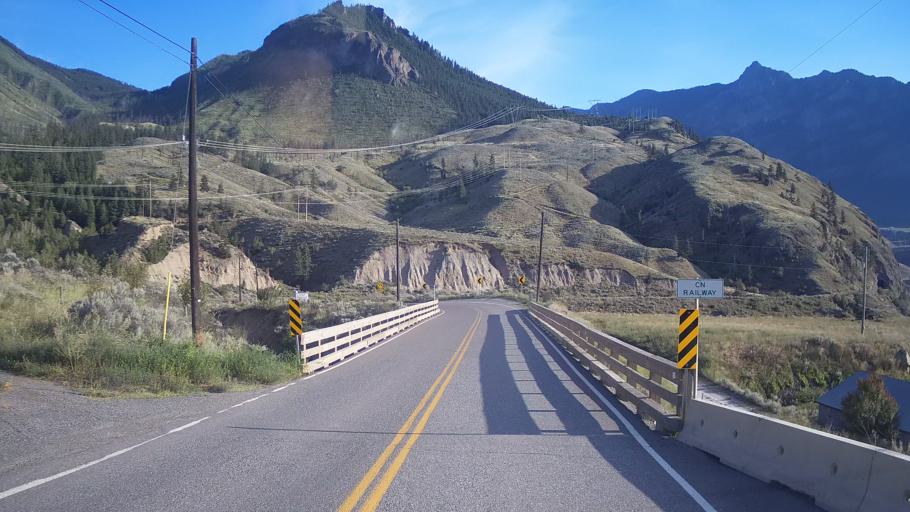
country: CA
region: British Columbia
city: Lillooet
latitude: 50.7582
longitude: -121.8335
